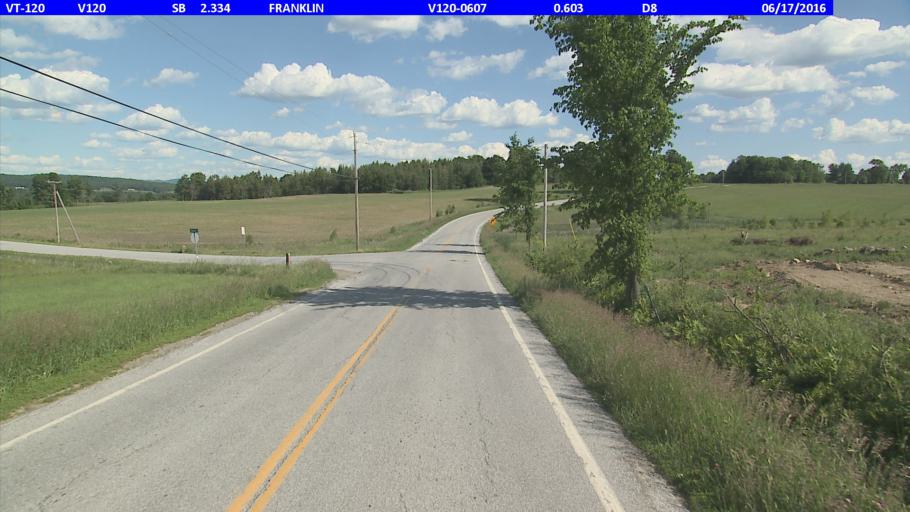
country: US
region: Vermont
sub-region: Franklin County
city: Enosburg Falls
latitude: 44.9430
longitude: -72.8995
